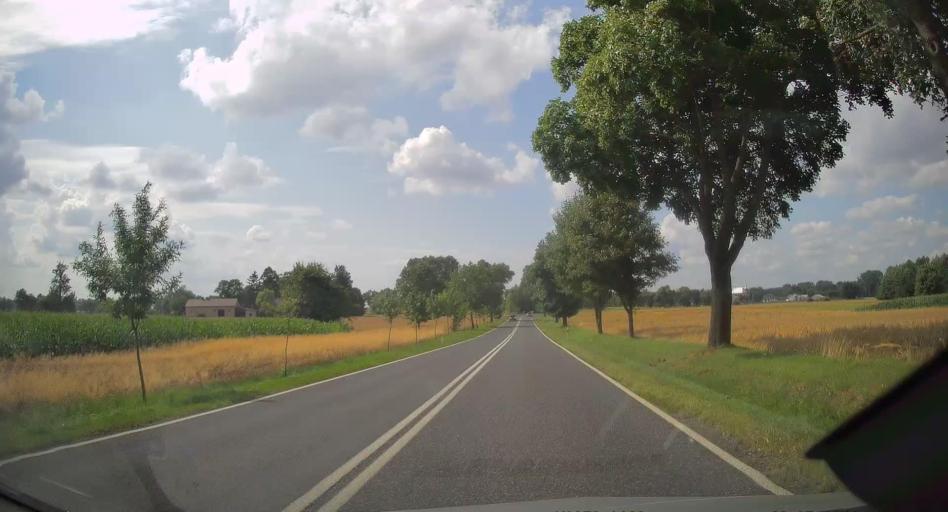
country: PL
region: Lodz Voivodeship
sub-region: Powiat brzezinski
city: Jezow
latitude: 51.8023
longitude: 20.0181
